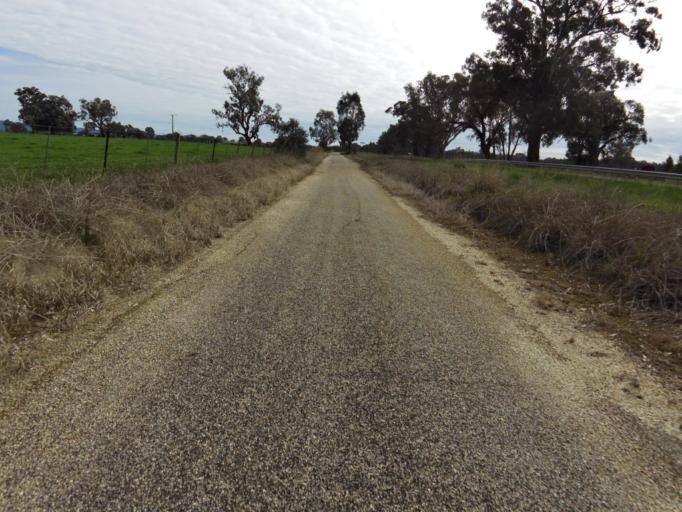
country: AU
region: Victoria
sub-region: Wangaratta
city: Wangaratta
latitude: -36.4185
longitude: 146.3557
